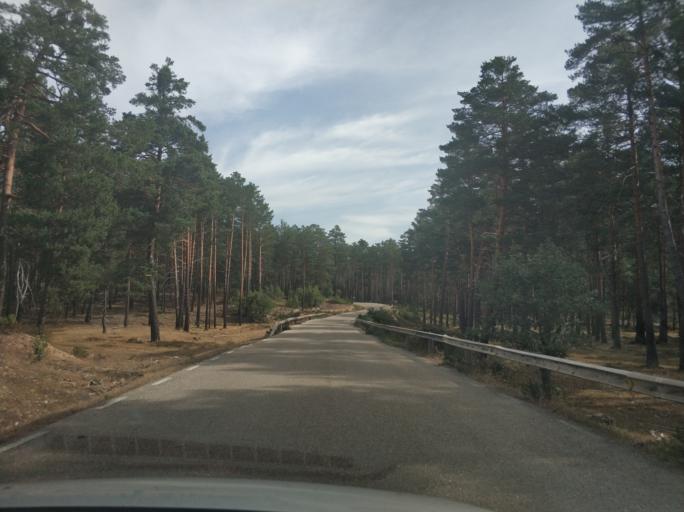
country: ES
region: Castille and Leon
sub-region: Provincia de Soria
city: Navaleno
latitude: 41.8718
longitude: -2.9404
